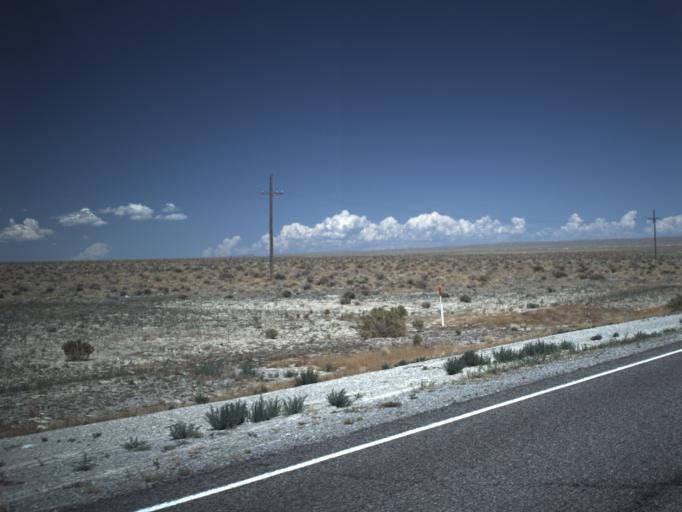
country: US
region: Utah
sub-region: Millard County
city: Delta
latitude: 39.0781
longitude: -113.2031
